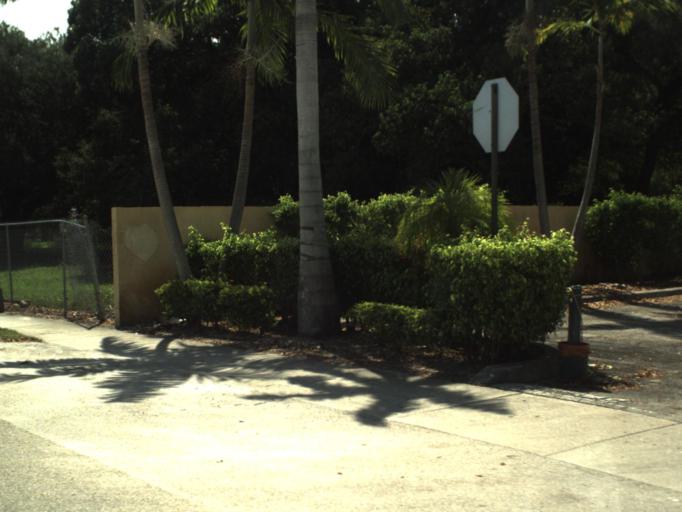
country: US
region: Florida
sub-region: Broward County
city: West Park
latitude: 25.9841
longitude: -80.1976
